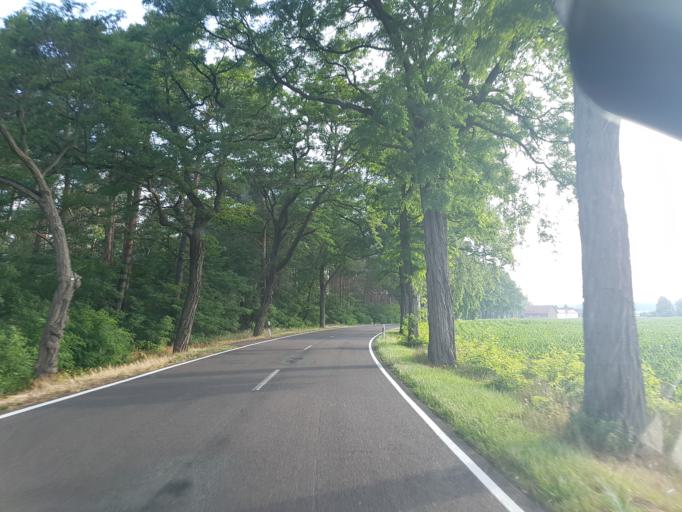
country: DE
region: Brandenburg
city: Schlieben
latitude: 51.7560
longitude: 13.3484
